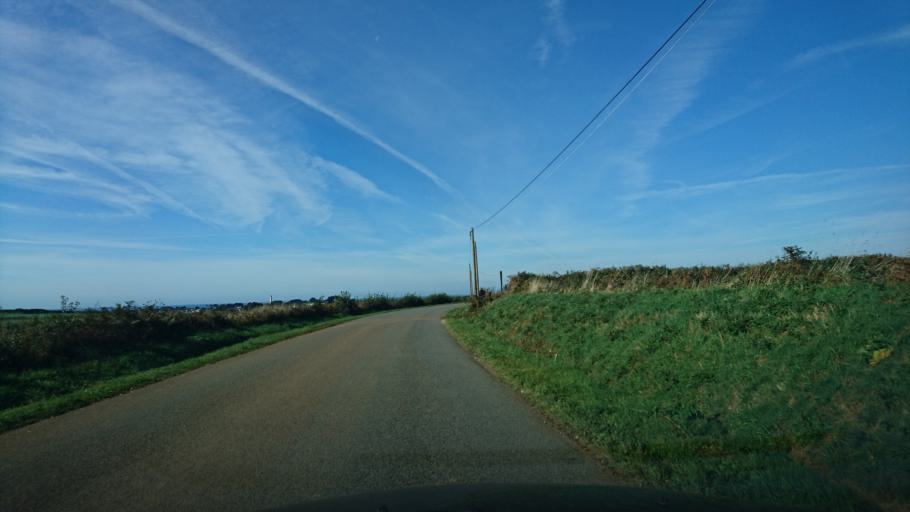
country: FR
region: Brittany
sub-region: Departement du Finistere
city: Plouarzel
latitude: 48.4277
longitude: -4.7508
